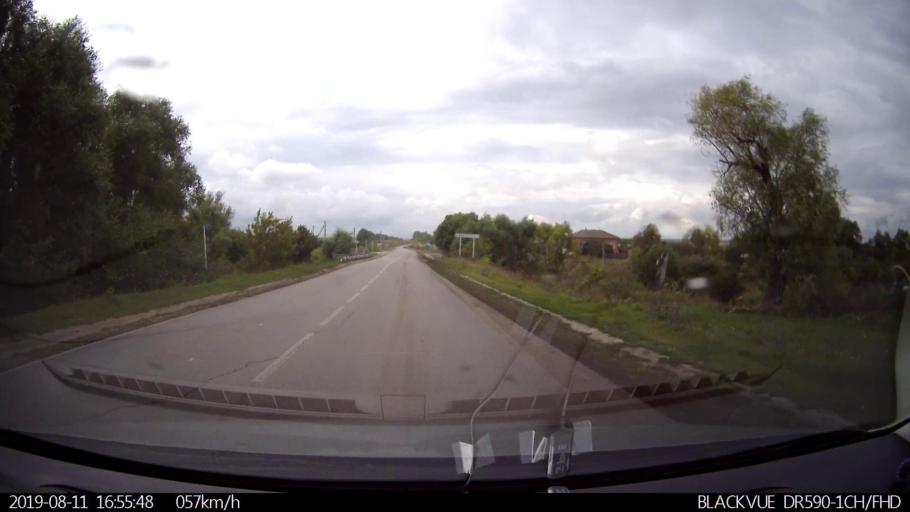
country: RU
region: Ulyanovsk
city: Mayna
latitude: 54.2839
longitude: 47.6601
